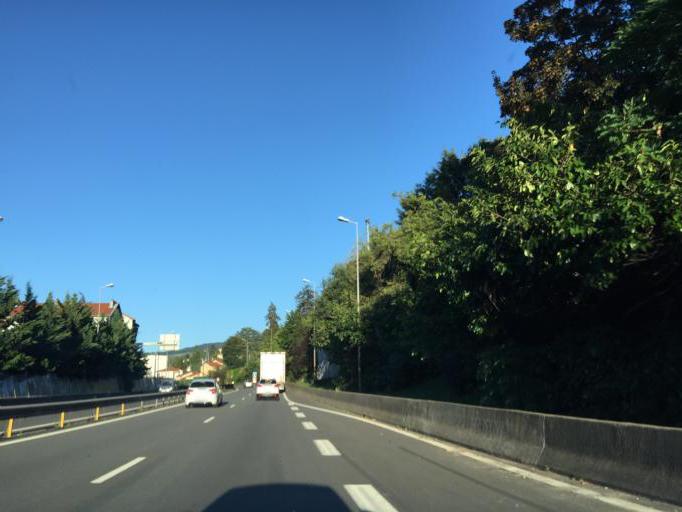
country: FR
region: Rhone-Alpes
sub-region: Departement de la Loire
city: Saint-Etienne
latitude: 45.4075
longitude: 4.3855
